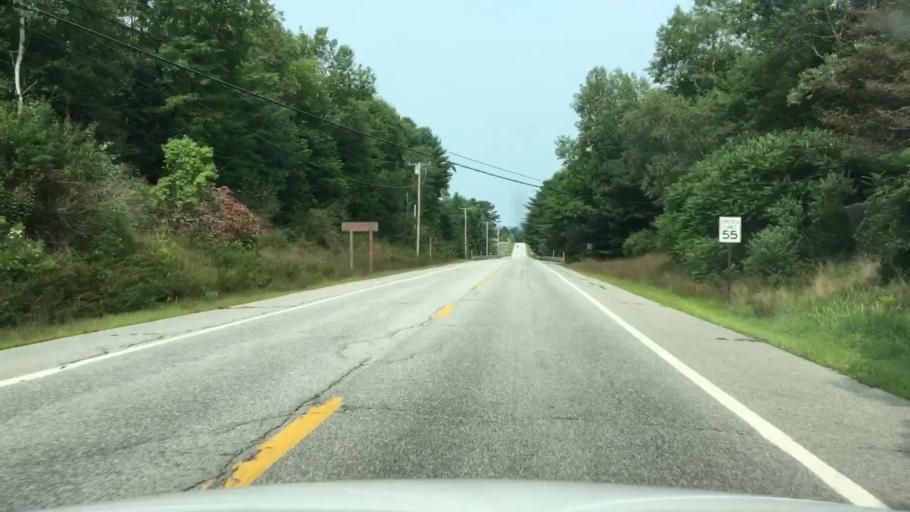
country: US
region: Maine
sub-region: Kennebec County
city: Wayne
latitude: 44.4051
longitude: -70.1322
